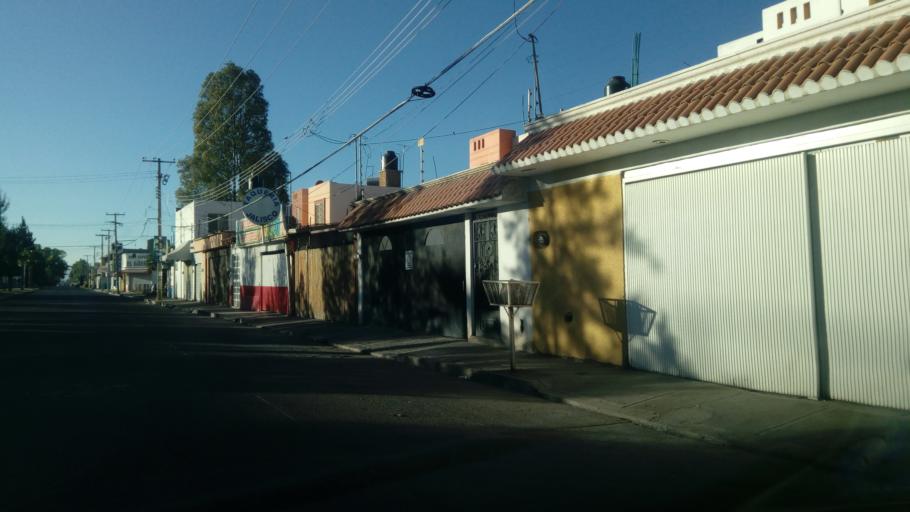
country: MX
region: Durango
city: Victoria de Durango
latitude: 24.0663
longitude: -104.6002
